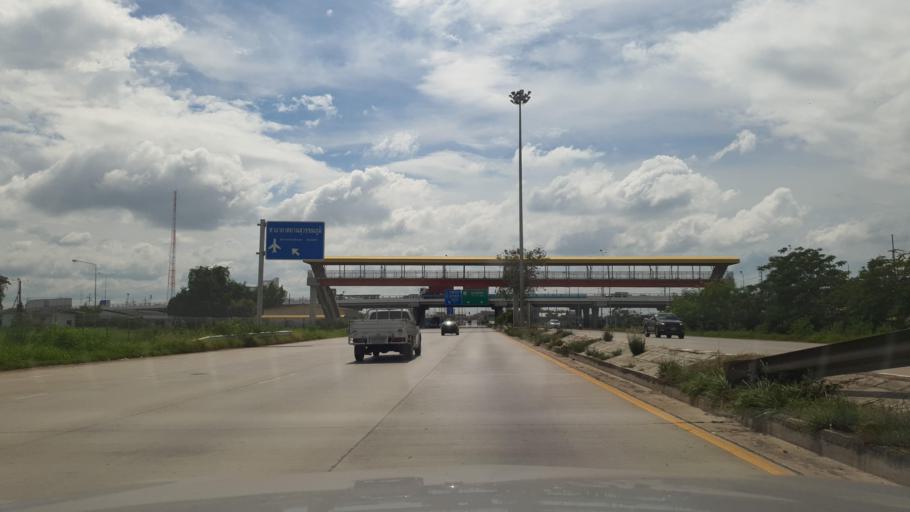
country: TH
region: Chachoengsao
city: Bang Pakong
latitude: 13.5591
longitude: 100.9944
